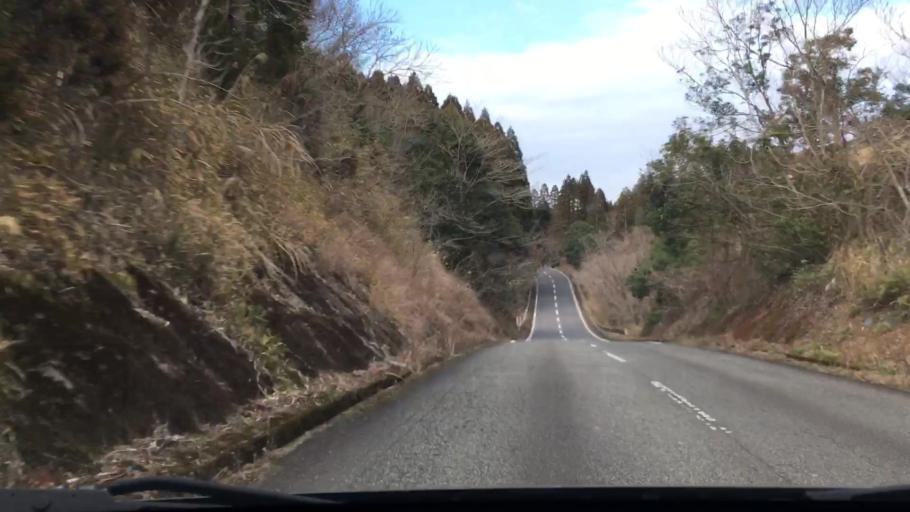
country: JP
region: Miyazaki
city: Nichinan
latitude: 31.7098
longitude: 131.3266
